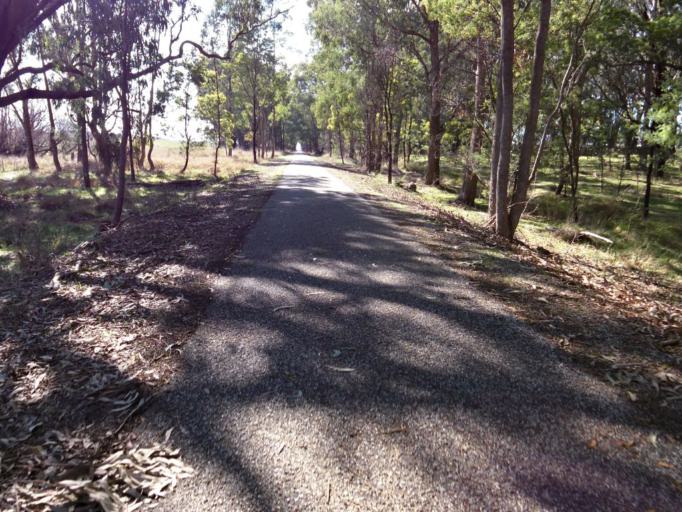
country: AU
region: Victoria
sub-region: Wangaratta
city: Wangaratta
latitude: -36.4013
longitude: 146.6442
